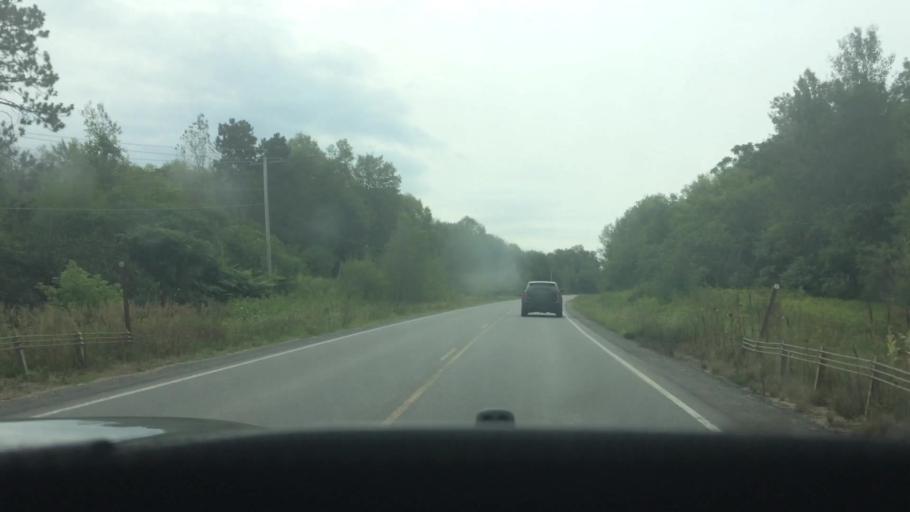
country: US
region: New York
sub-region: St. Lawrence County
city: Canton
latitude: 44.4806
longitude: -75.2438
